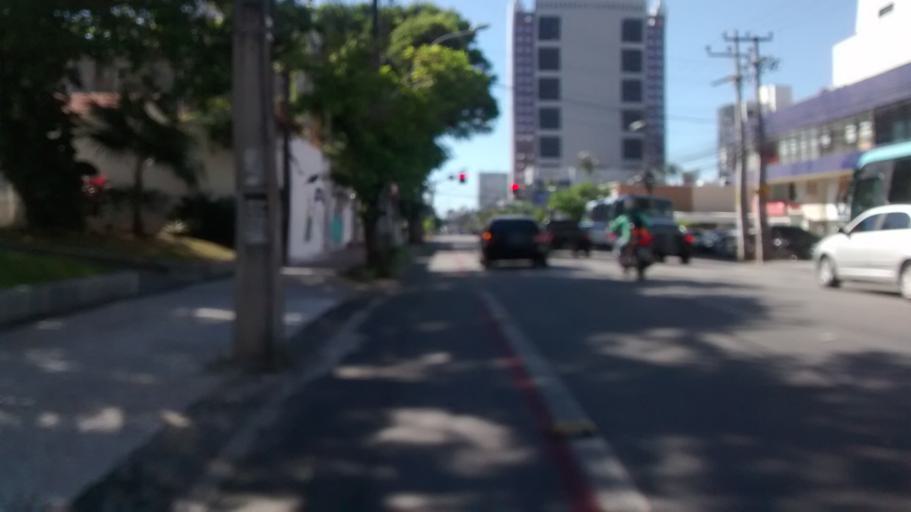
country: BR
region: Ceara
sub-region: Fortaleza
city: Fortaleza
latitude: -3.7350
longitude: -38.5020
